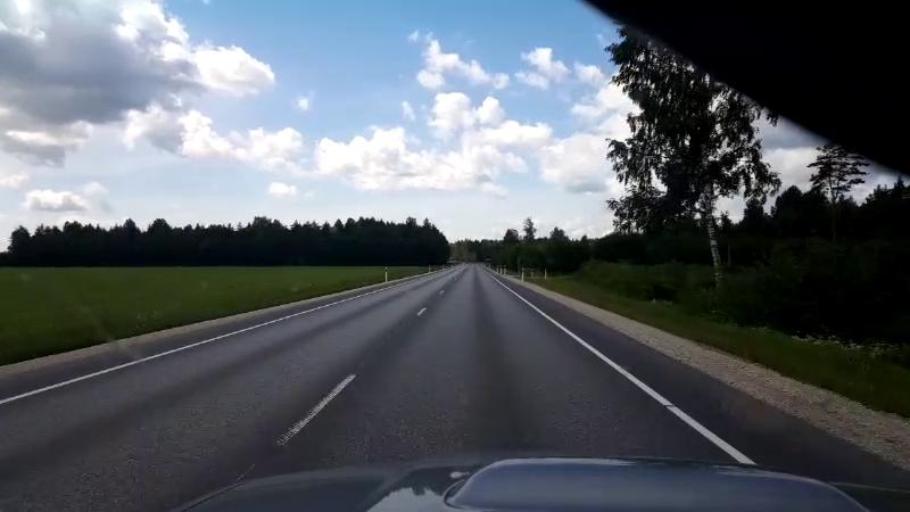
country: EE
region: Jaervamaa
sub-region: Paide linn
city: Paide
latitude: 59.0085
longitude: 25.6892
